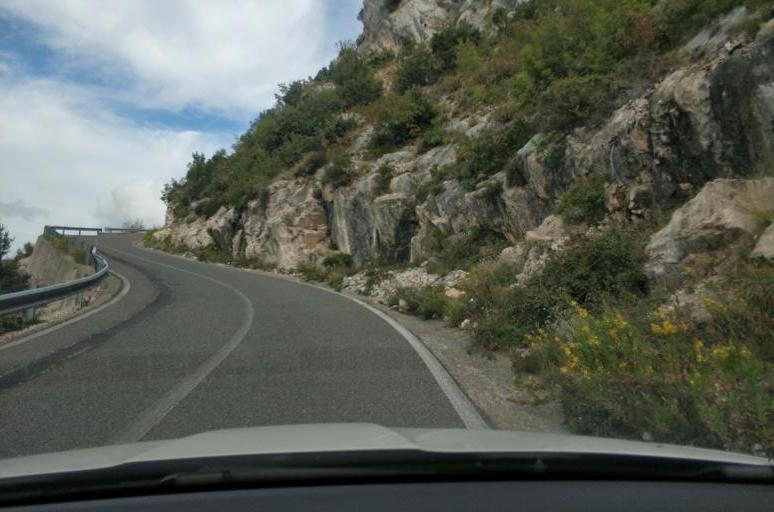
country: AL
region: Durres
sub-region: Rrethi i Krujes
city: Kruje
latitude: 41.5265
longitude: 19.7943
